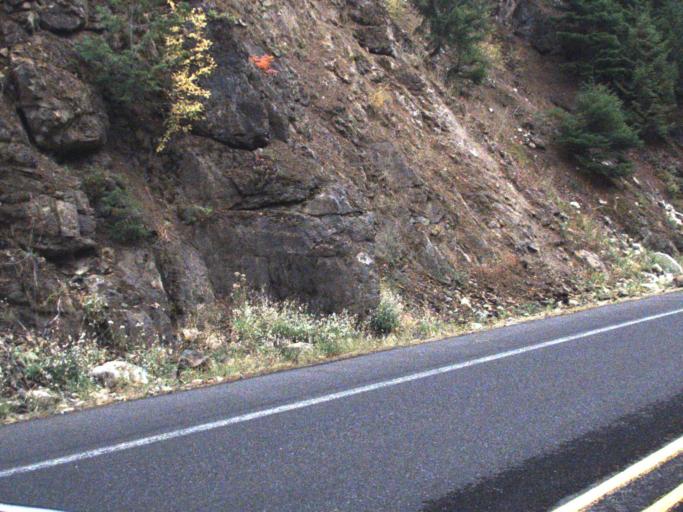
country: US
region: Washington
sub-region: Pierce County
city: Buckley
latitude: 46.6684
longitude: -121.4876
